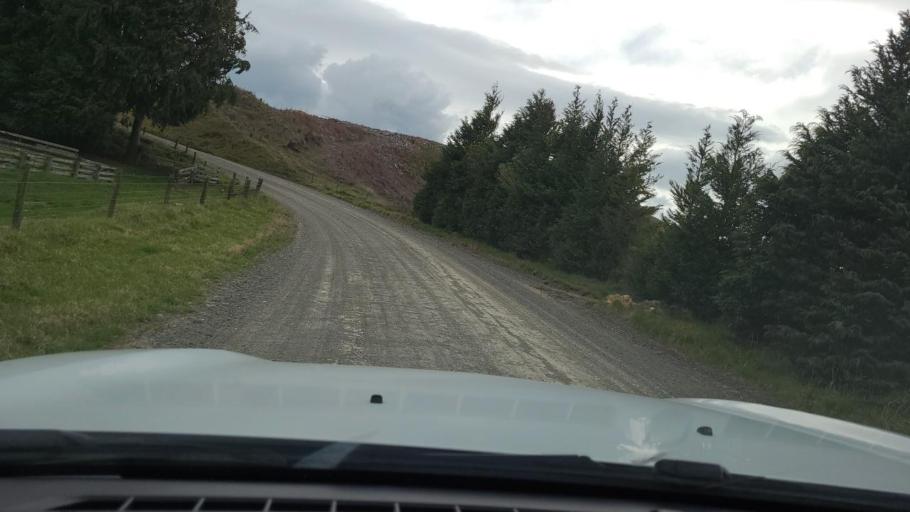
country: NZ
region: Hawke's Bay
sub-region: Napier City
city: Napier
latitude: -39.3117
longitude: 176.8353
